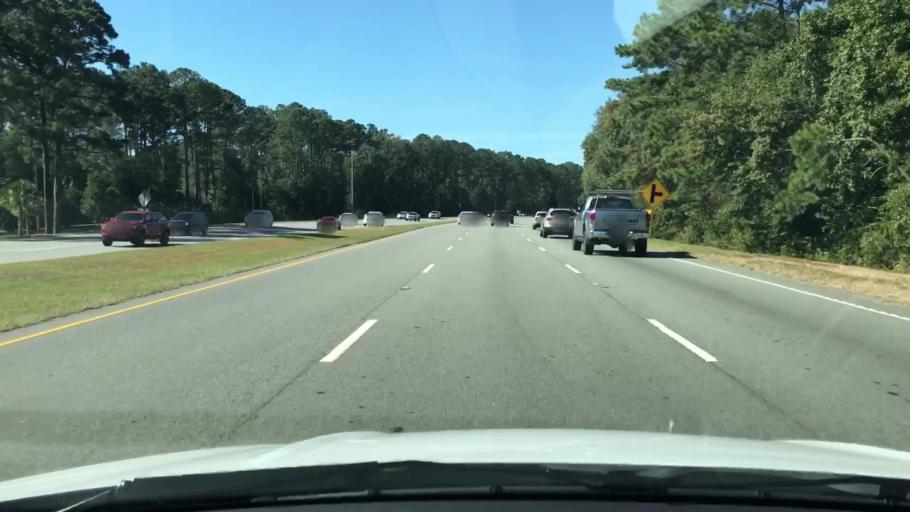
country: US
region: South Carolina
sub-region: Beaufort County
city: Bluffton
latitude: 32.2866
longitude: -80.8899
